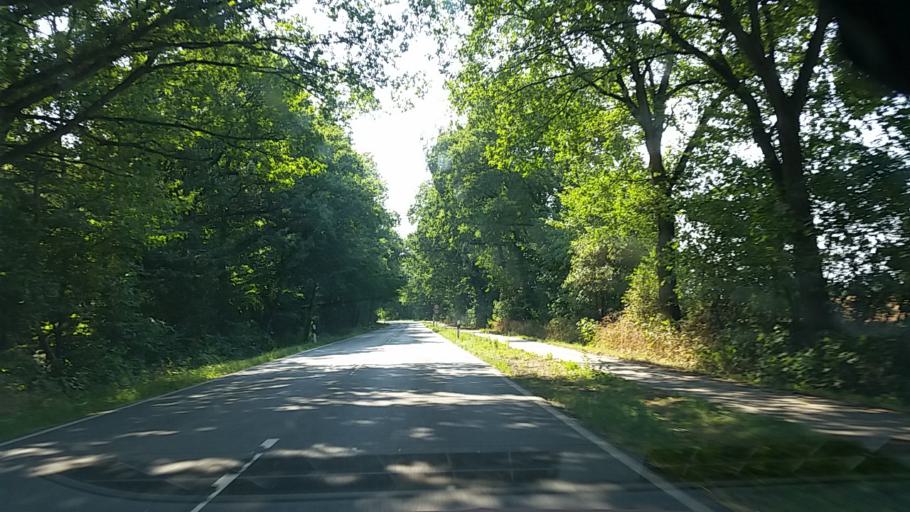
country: DE
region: Schleswig-Holstein
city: Grande
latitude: 53.5770
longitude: 10.3755
